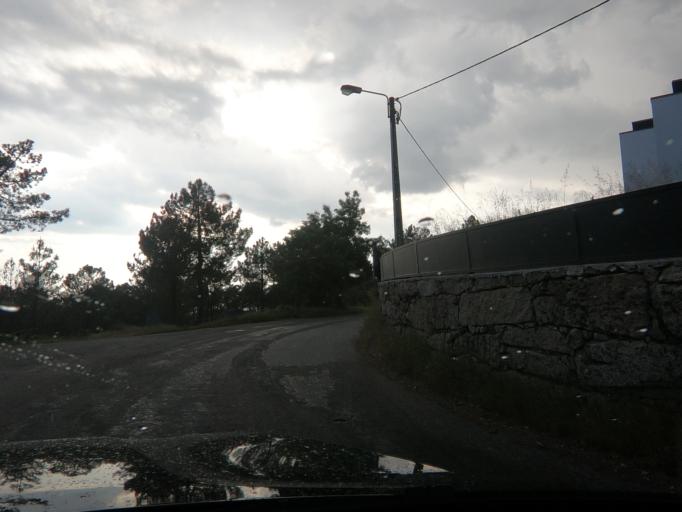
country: PT
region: Vila Real
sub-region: Vila Real
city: Vila Real
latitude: 41.3181
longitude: -7.6755
